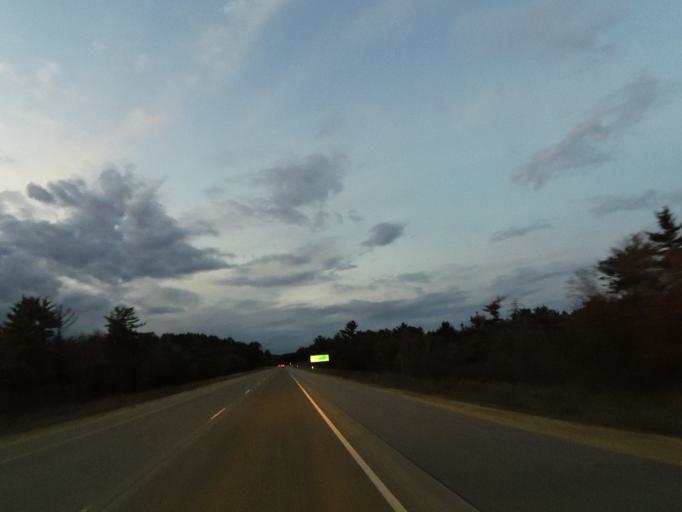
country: US
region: Wisconsin
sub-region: Monroe County
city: Tomah
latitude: 44.0334
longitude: -90.5123
